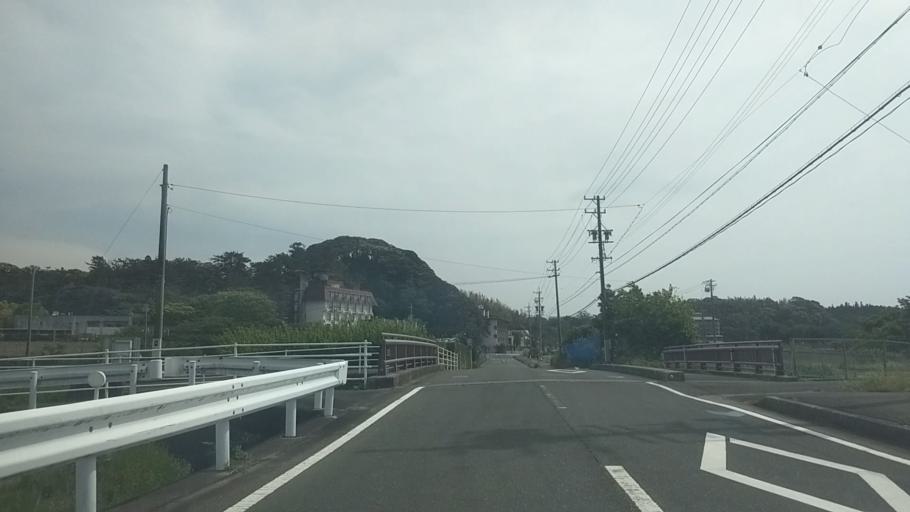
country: JP
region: Shizuoka
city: Kosai-shi
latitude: 34.7689
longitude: 137.6299
